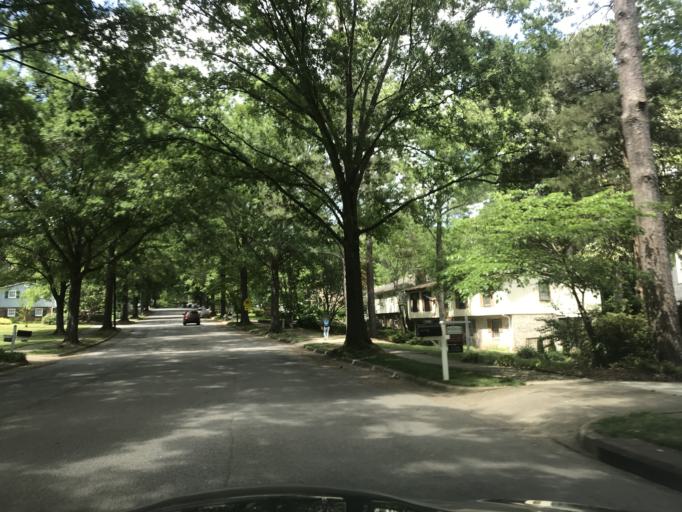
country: US
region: North Carolina
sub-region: Wake County
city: West Raleigh
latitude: 35.8541
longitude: -78.6302
